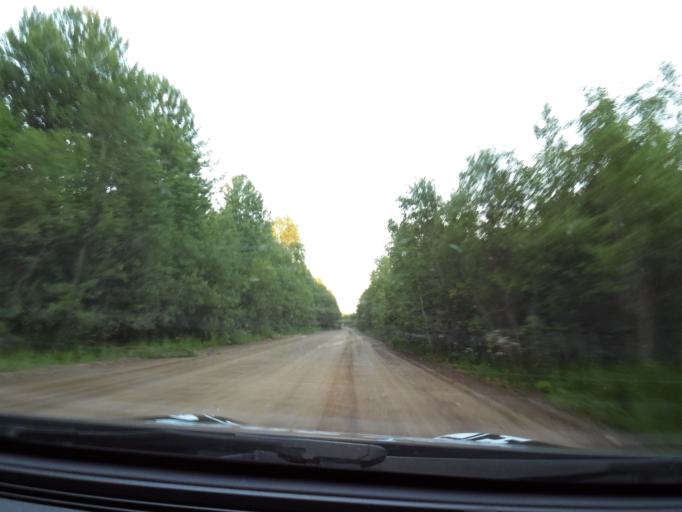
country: RU
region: Leningrad
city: Voznesen'ye
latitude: 60.9169
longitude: 35.4841
